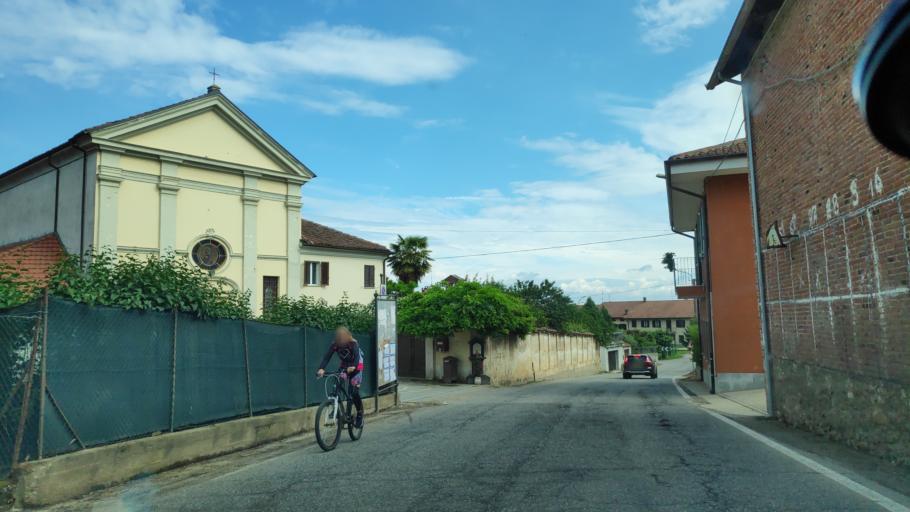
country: IT
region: Piedmont
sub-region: Provincia di Torino
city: Pecetto
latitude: 45.0064
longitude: 7.7623
